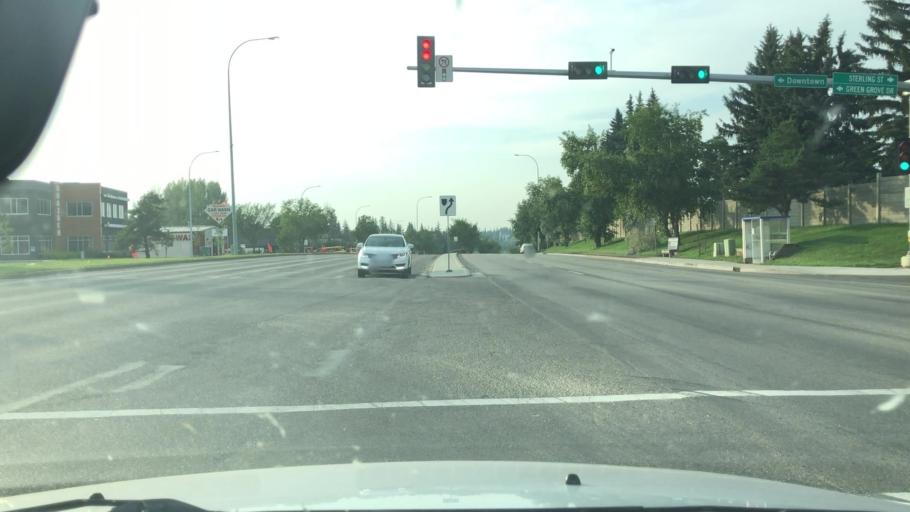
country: CA
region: Alberta
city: St. Albert
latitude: 53.6275
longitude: -113.6186
